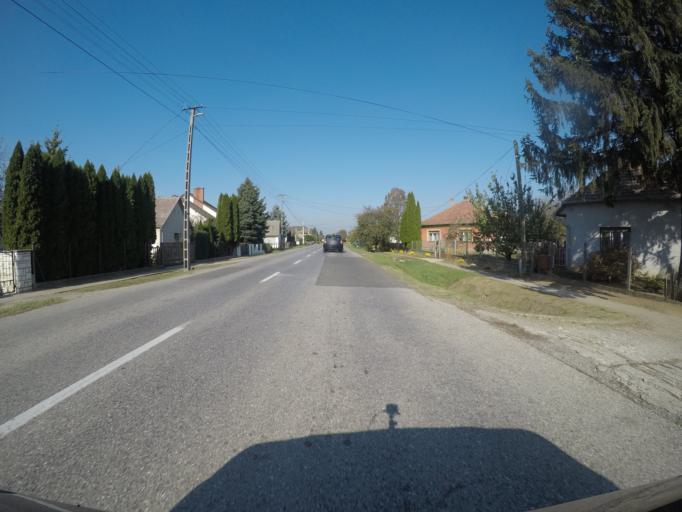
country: HU
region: Tolna
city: Szedres
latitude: 46.4792
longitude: 18.6834
